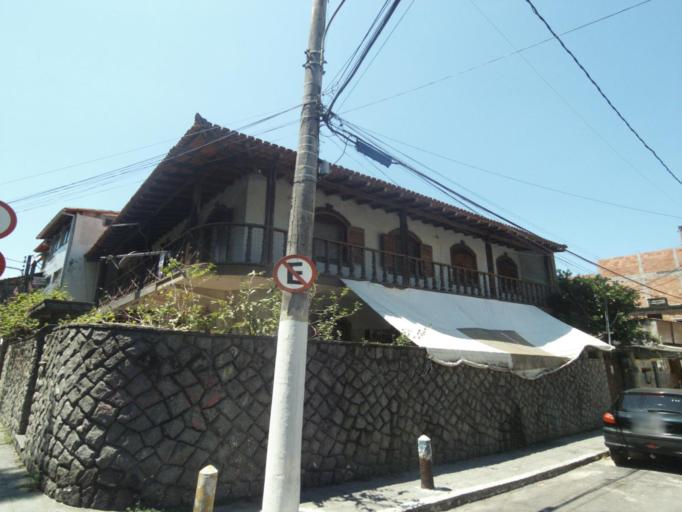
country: BR
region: Rio de Janeiro
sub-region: Niteroi
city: Niteroi
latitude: -22.9266
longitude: -43.1203
